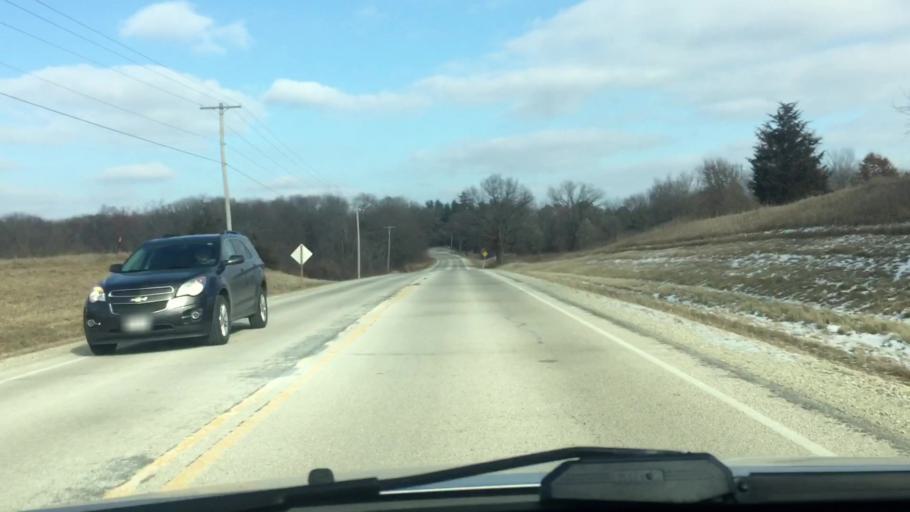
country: US
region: Wisconsin
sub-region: Jefferson County
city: Palmyra
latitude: 42.8863
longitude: -88.5585
